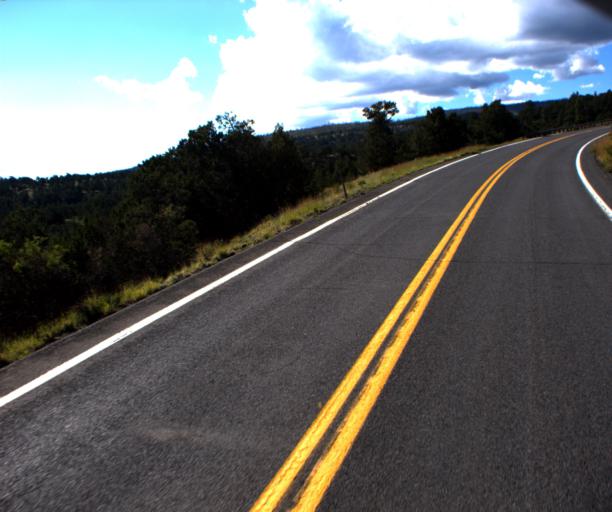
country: US
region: Arizona
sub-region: Apache County
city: Eagar
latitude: 34.0861
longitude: -109.3436
